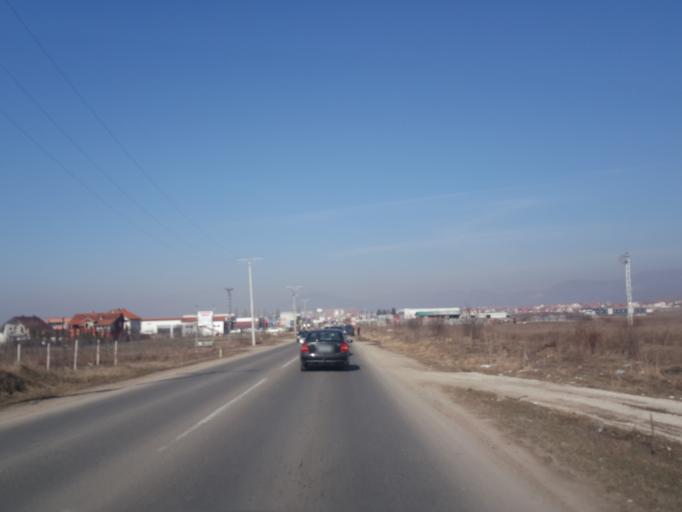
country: XK
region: Mitrovica
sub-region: Vushtrri
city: Vushtrri
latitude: 42.8042
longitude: 20.9921
